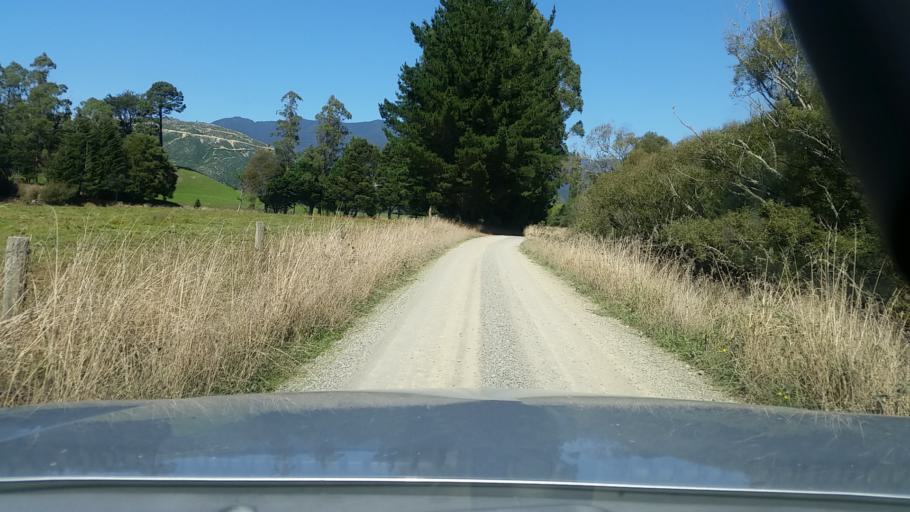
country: NZ
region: Nelson
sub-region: Nelson City
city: Nelson
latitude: -41.2626
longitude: 173.5765
